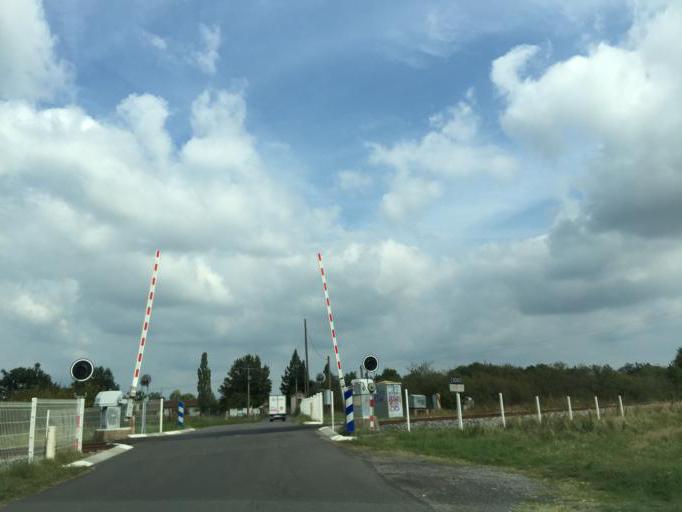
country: FR
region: Rhone-Alpes
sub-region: Departement de la Loire
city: Sury-le-Comtal
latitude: 45.5387
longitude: 4.1579
